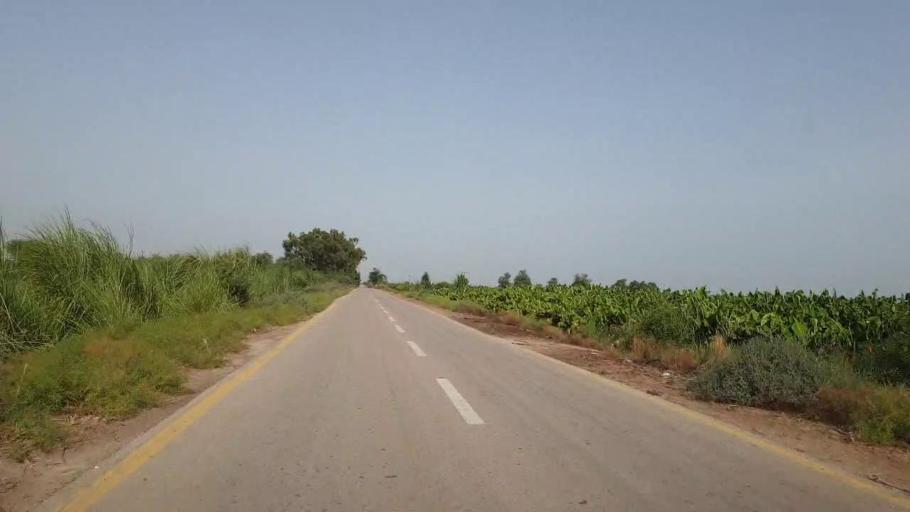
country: PK
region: Sindh
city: Bandhi
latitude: 26.5883
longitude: 68.2234
